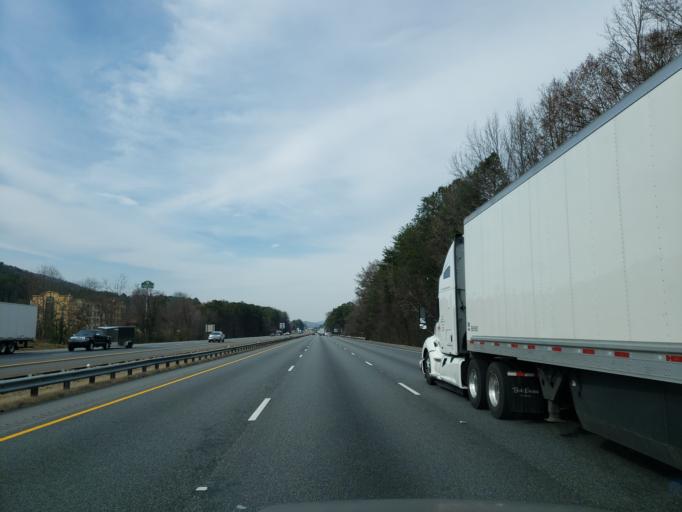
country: US
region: Georgia
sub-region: Whitfield County
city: Dalton
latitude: 34.7661
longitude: -85.0016
